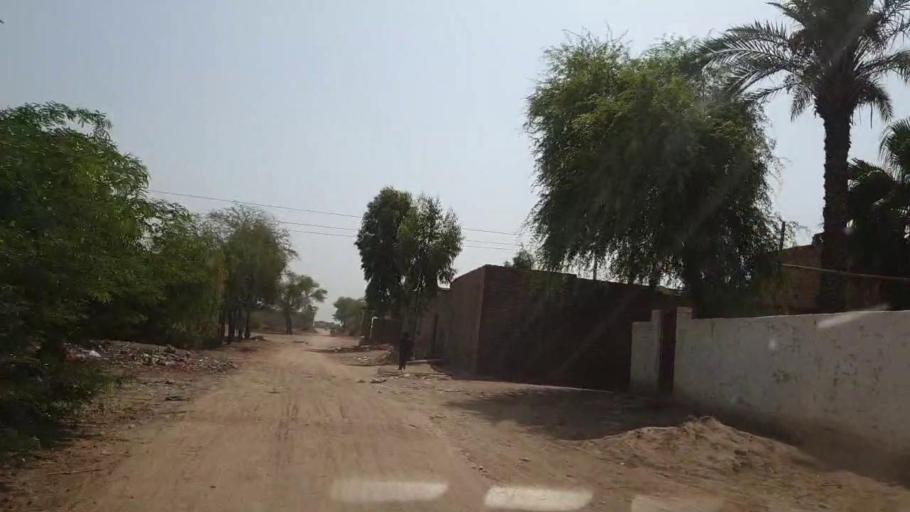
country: PK
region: Sindh
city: Lakhi
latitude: 27.8803
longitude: 68.6796
